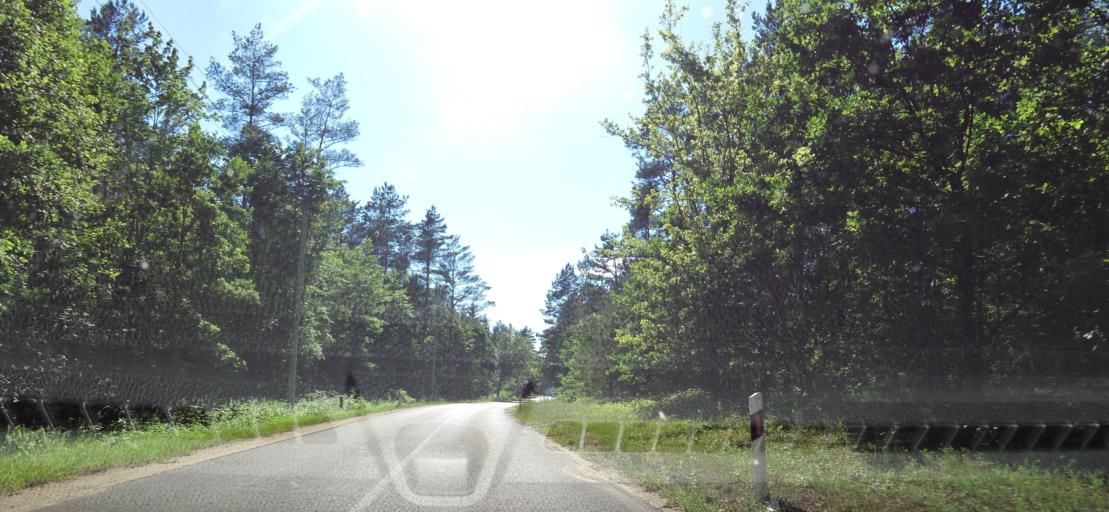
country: LT
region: Vilnius County
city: Rasos
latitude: 54.7520
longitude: 25.3291
